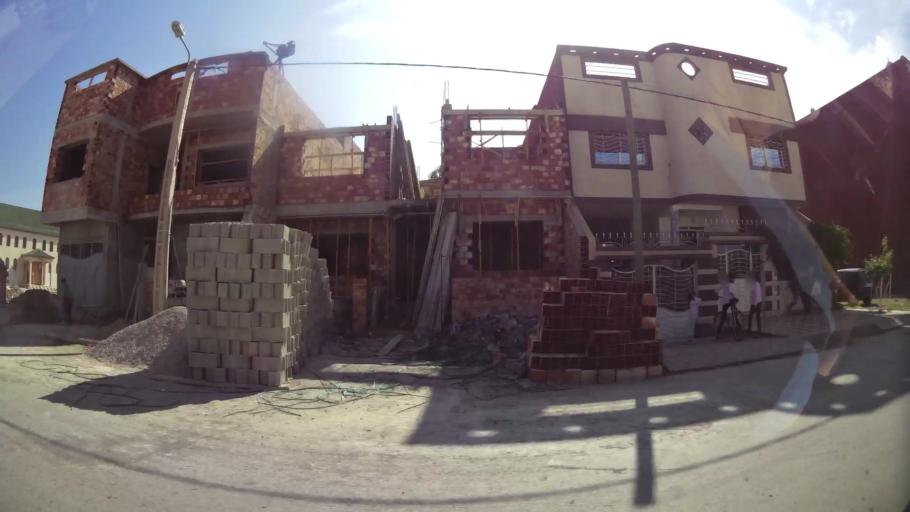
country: MA
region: Oriental
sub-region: Oujda-Angad
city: Oujda
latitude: 34.6970
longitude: -1.8822
